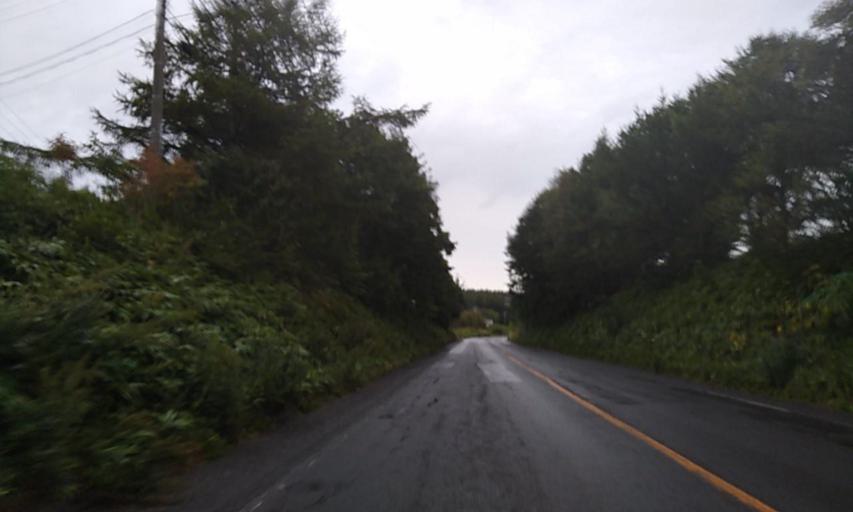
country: JP
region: Hokkaido
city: Mombetsu
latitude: 44.4823
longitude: 143.1012
